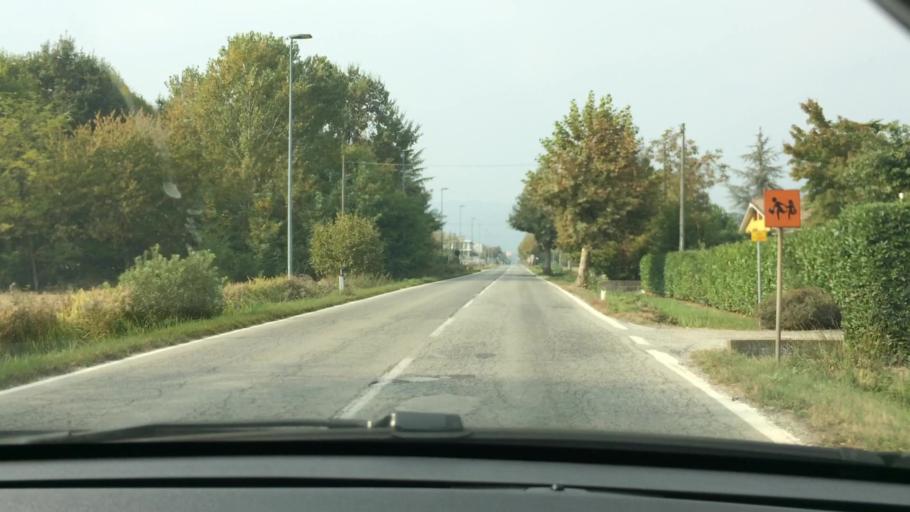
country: IT
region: Piedmont
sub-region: Provincia di Torino
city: Cumiana
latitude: 44.9631
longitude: 7.3992
